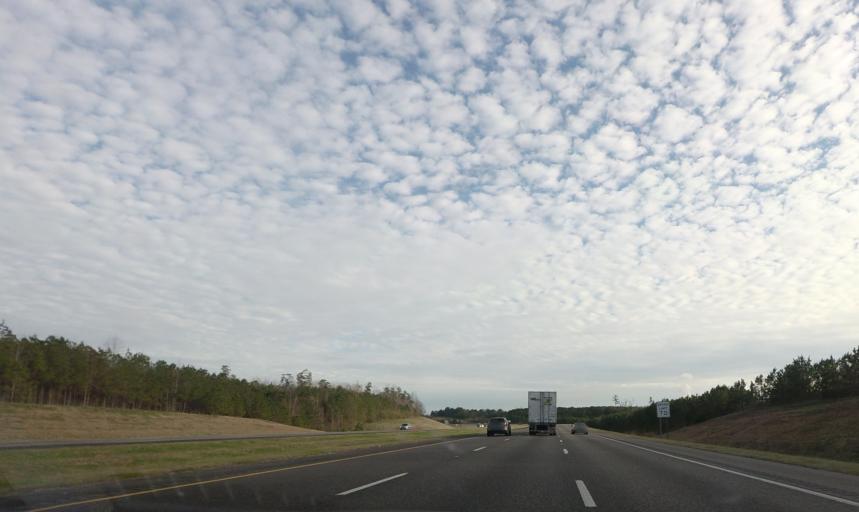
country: US
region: Alabama
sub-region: Walker County
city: Dora
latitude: 33.6699
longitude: -87.0736
